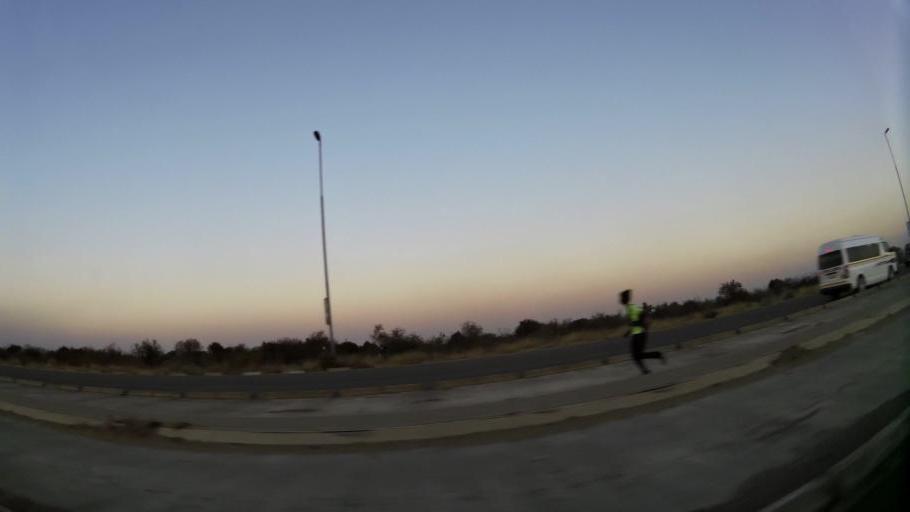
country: ZA
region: North-West
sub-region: Bojanala Platinum District Municipality
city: Rustenburg
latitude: -25.6417
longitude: 27.2623
